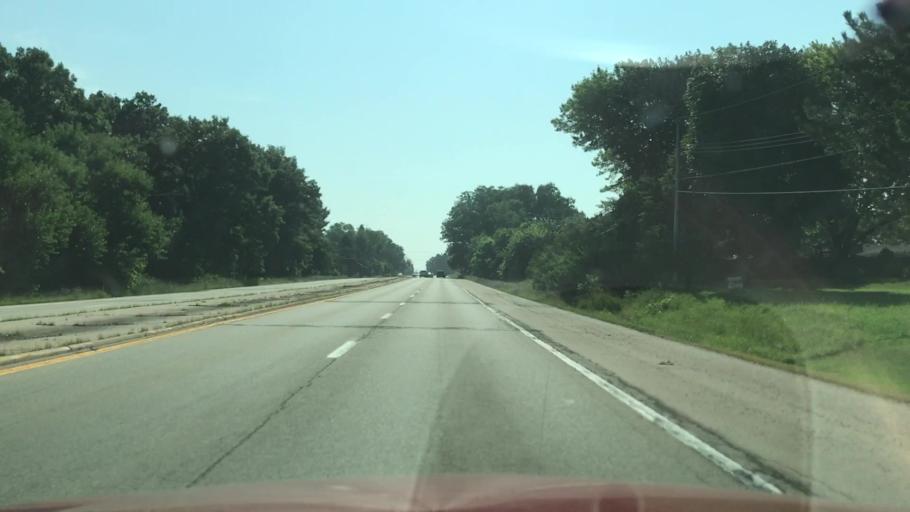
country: US
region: Illinois
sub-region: Winnebago County
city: Cherry Valley
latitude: 42.2385
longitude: -88.9925
